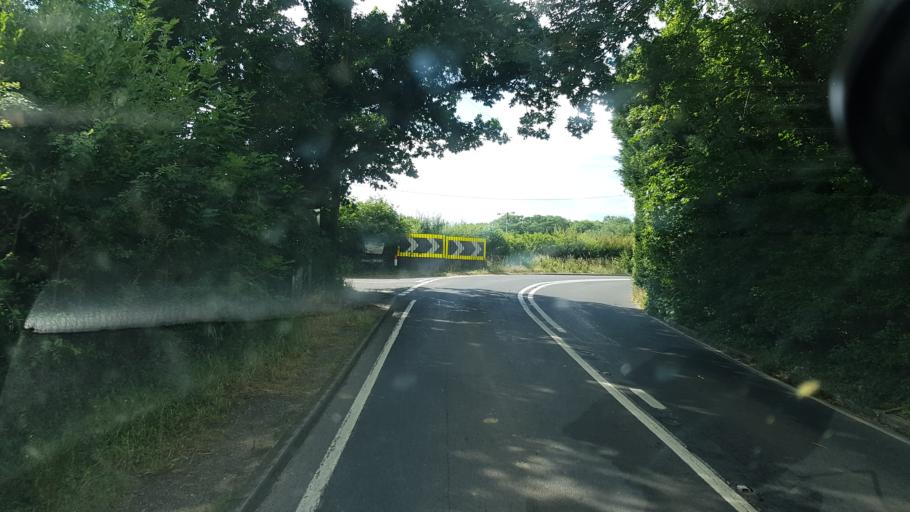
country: GB
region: England
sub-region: West Sussex
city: Billingshurst
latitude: 51.0002
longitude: -0.4237
